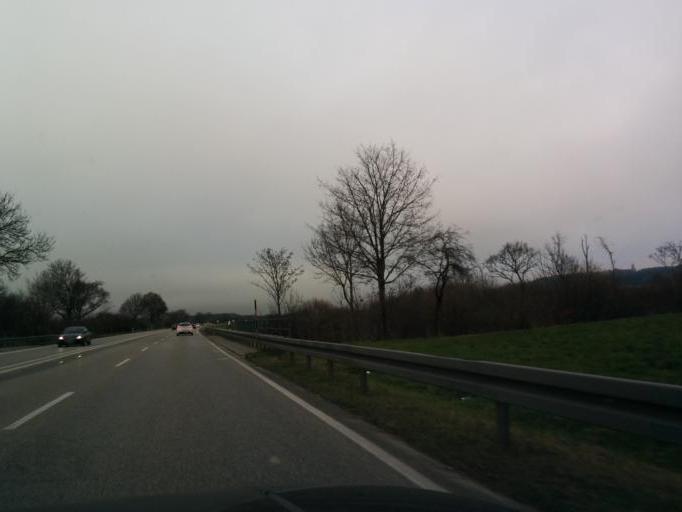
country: DE
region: Bavaria
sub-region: Swabia
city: Rieden
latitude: 47.9374
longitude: 10.6635
